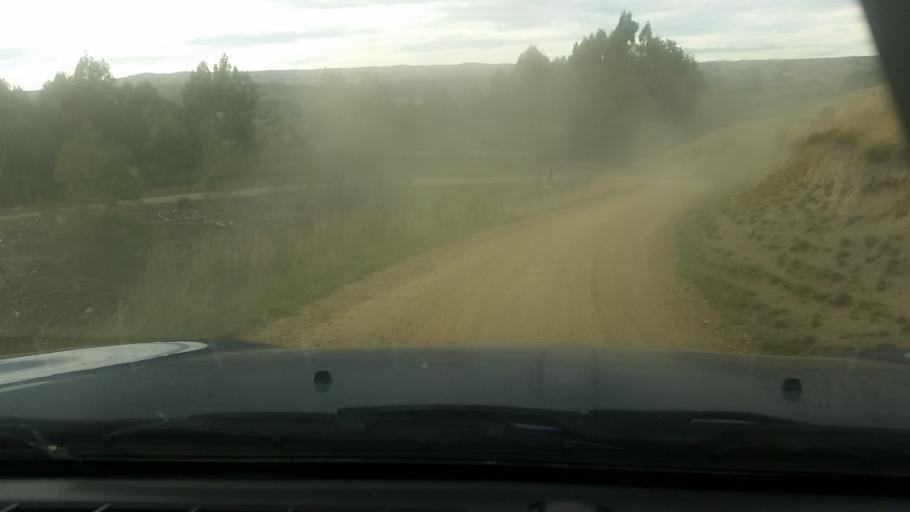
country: NZ
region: Otago
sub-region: Clutha District
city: Balclutha
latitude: -45.6804
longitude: 169.4955
